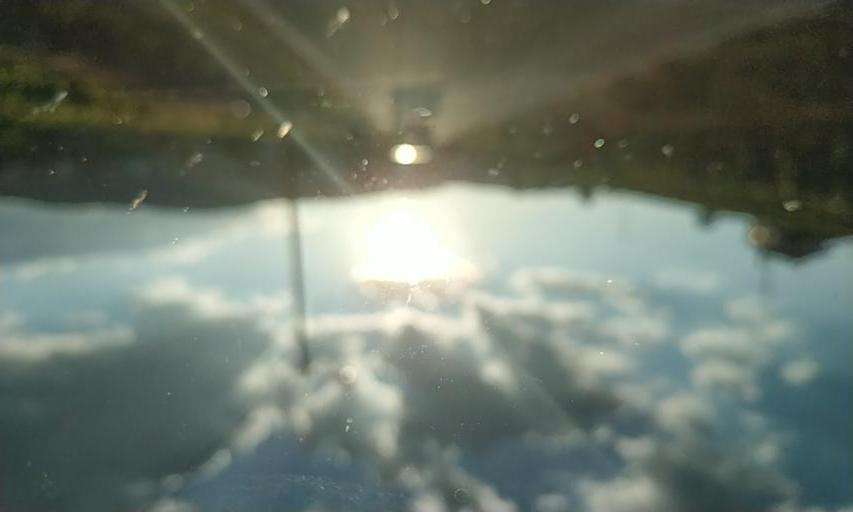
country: PT
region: Vila Real
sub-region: Sabrosa
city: Sabrosa
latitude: 41.2766
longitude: -7.4653
